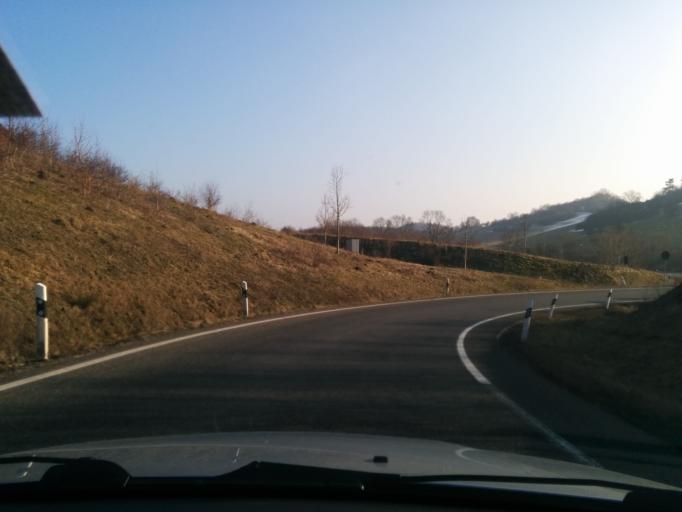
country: DE
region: Hesse
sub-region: Regierungsbezirk Kassel
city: Grossalmerode
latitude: 51.1912
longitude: 9.7902
